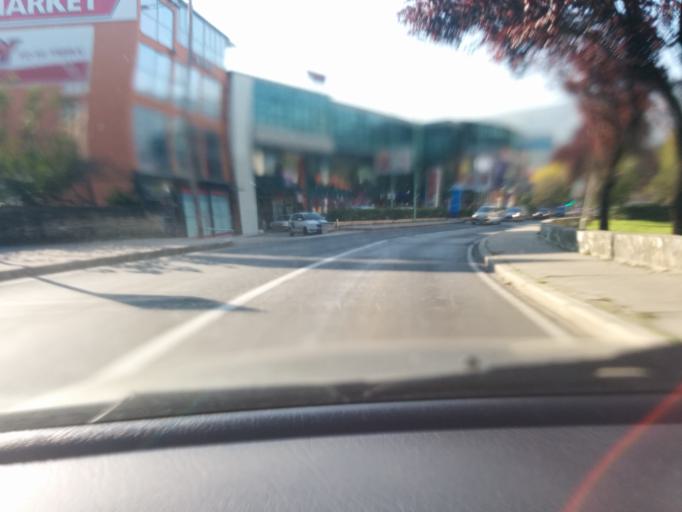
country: HR
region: Splitsko-Dalmatinska
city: Sinj
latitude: 43.6997
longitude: 16.6414
